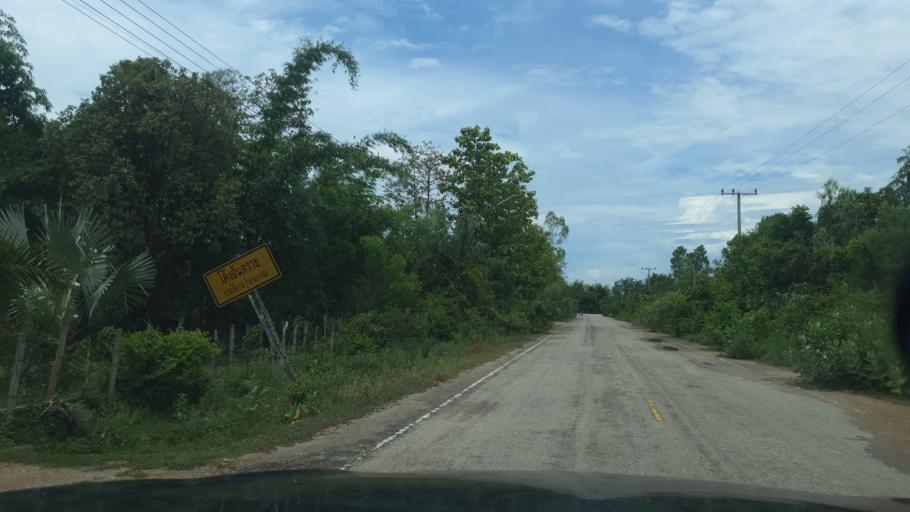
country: TH
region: Lampang
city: Ko Kha
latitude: 18.2380
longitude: 99.3691
